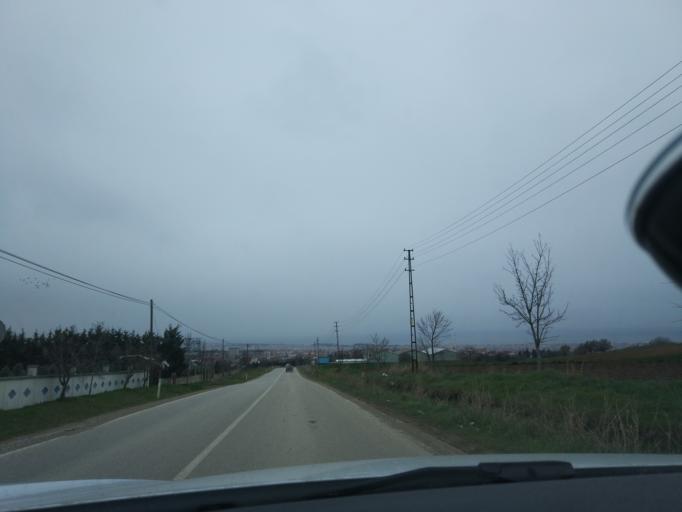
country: TR
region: Tekirdag
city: Marmara Ereglisi
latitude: 41.0228
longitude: 27.8529
